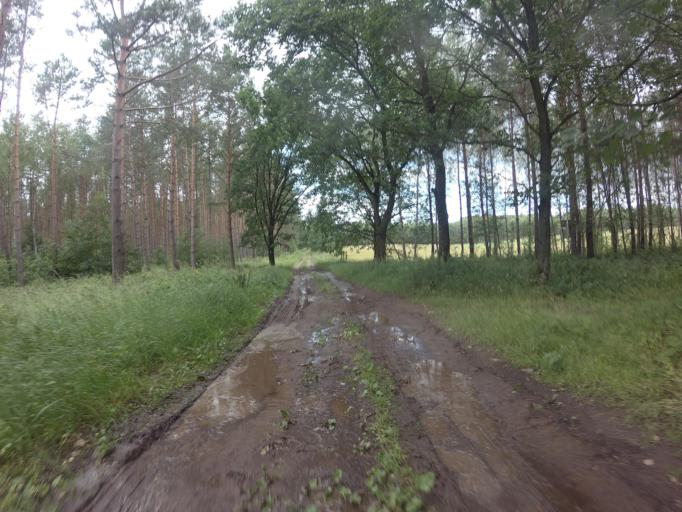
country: PL
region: West Pomeranian Voivodeship
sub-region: Powiat choszczenski
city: Krzecin
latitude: 53.0393
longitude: 15.5687
